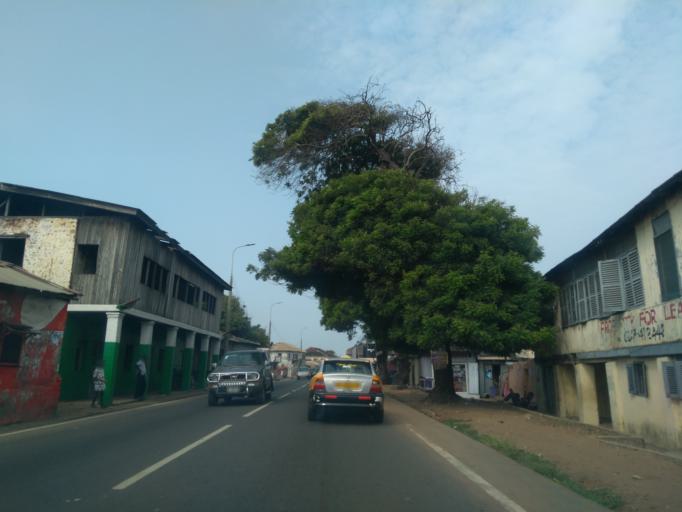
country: GH
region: Greater Accra
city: Accra
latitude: 5.5505
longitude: -0.1851
